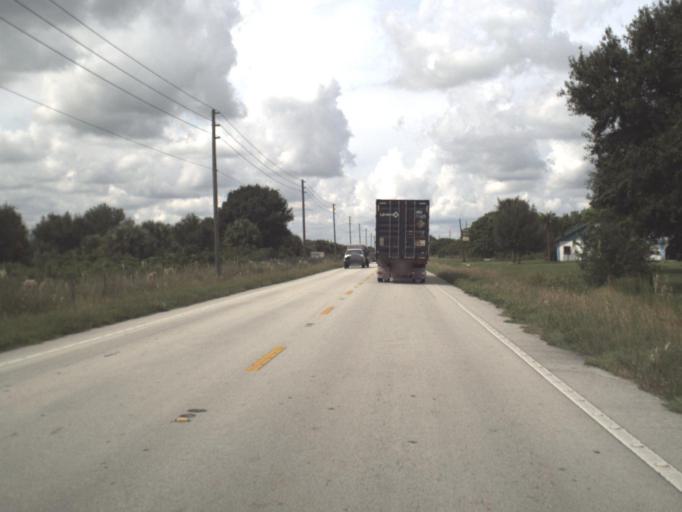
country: US
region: Florida
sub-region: Okeechobee County
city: Okeechobee
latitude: 27.2436
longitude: -80.8680
